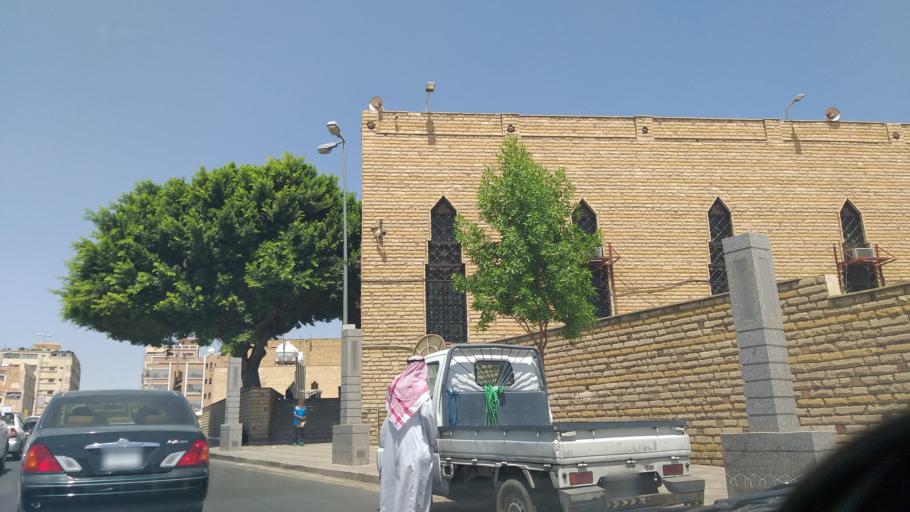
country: SA
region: Makkah
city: Ta'if
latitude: 21.2699
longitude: 40.4093
